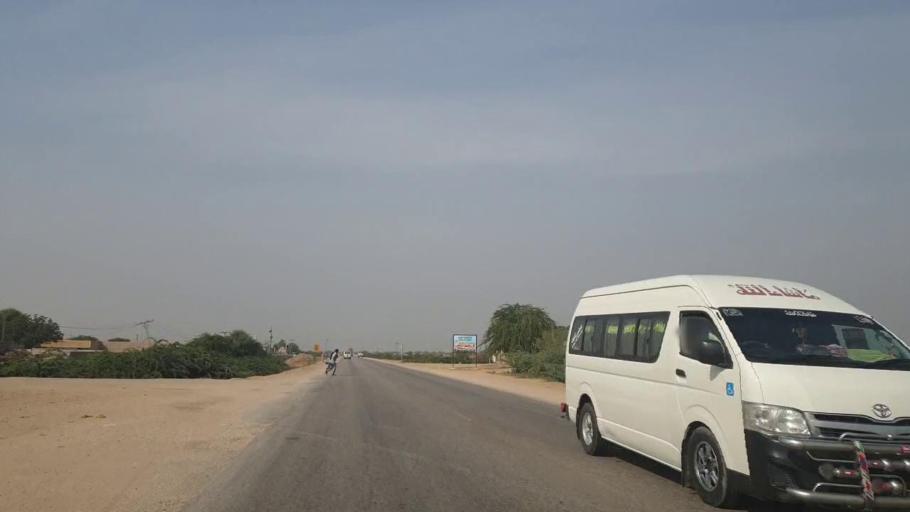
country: PK
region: Sindh
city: Sann
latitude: 26.0595
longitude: 68.1042
